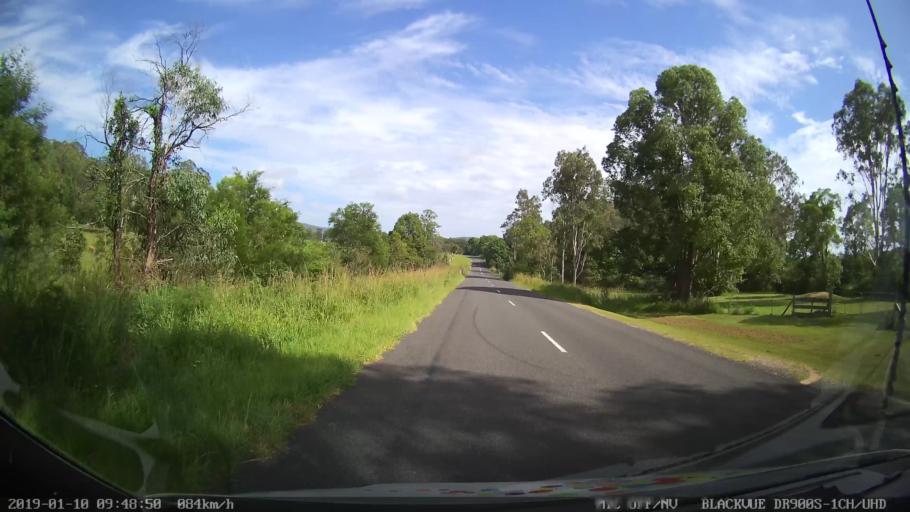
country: AU
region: New South Wales
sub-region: Coffs Harbour
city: Nana Glen
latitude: -30.0680
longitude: 152.9844
